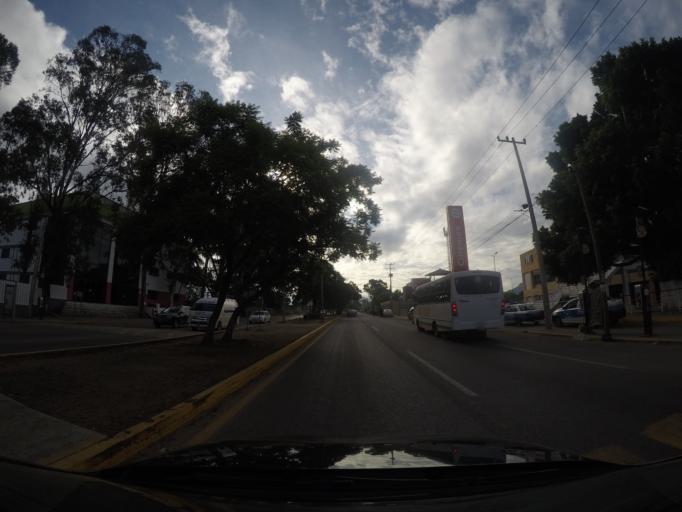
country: MX
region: Oaxaca
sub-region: Santa Cruz Amilpas
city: Santa Cruz Amilpas
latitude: 17.0688
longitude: -96.6947
